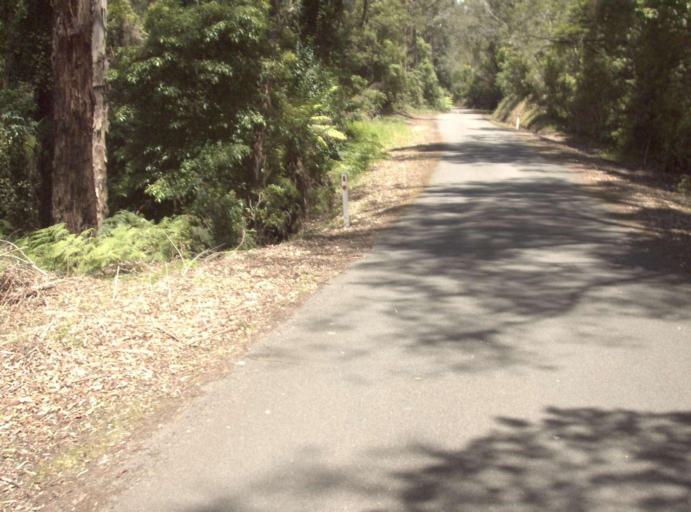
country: AU
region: New South Wales
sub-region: Bombala
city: Bombala
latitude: -37.4922
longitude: 148.9255
